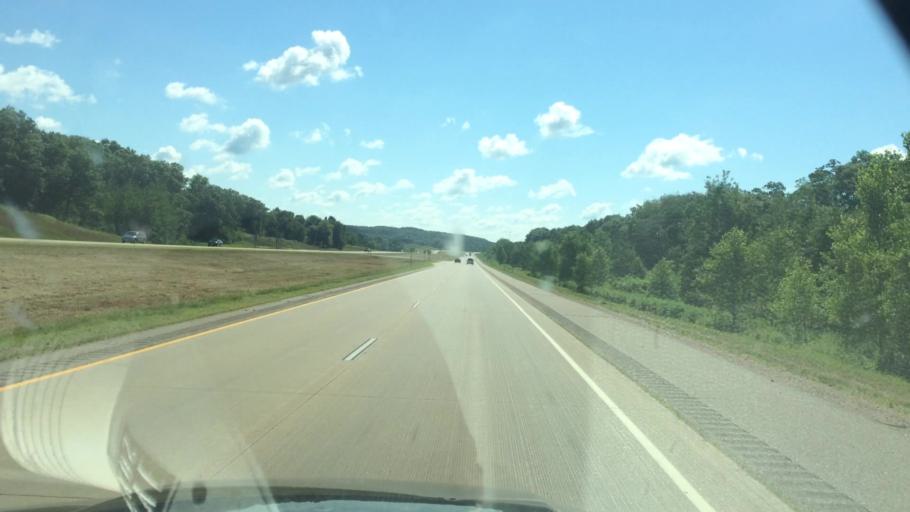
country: US
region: Wisconsin
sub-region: Portage County
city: Amherst
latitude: 44.5017
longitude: -89.3993
